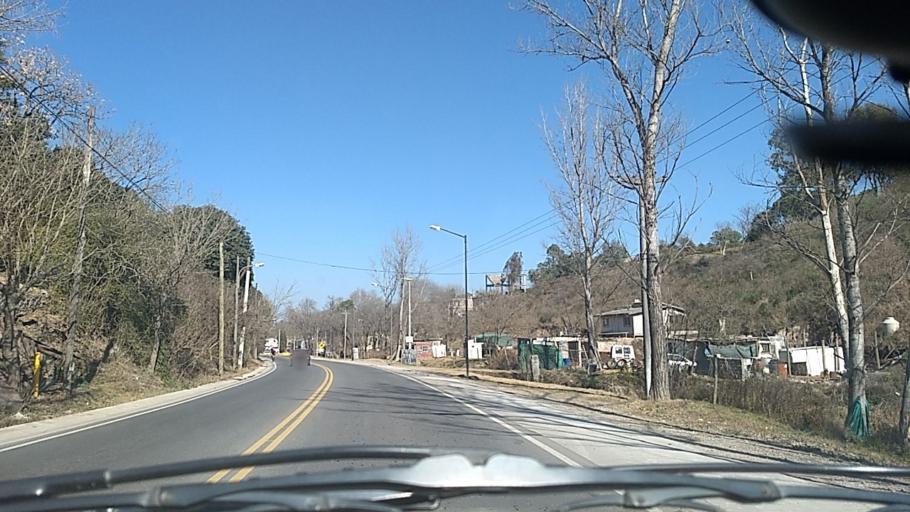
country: AR
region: Cordoba
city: Agua de Oro
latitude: -31.1014
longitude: -64.2917
